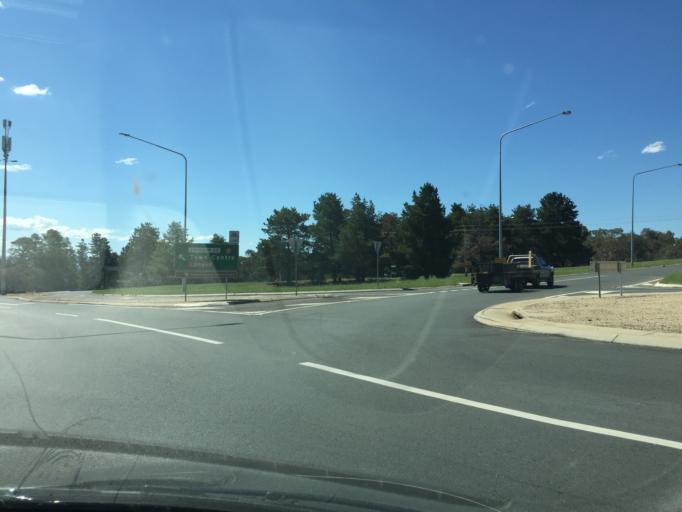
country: AU
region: Australian Capital Territory
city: Macarthur
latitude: -35.4365
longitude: 149.1254
